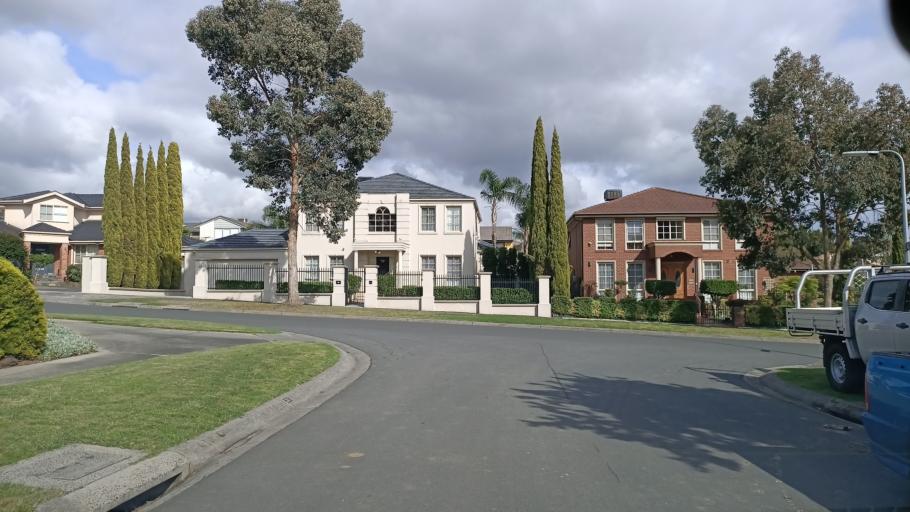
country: AU
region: Victoria
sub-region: Monash
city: Mulgrave
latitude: -37.9271
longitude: 145.1993
